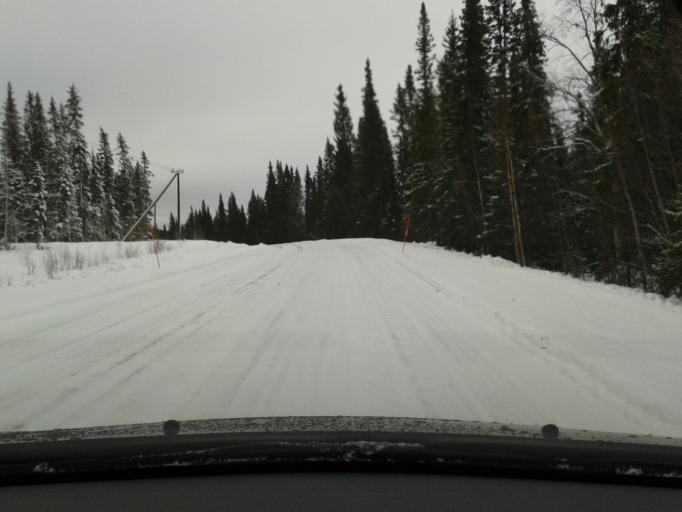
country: SE
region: Vaesterbotten
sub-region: Vilhelmina Kommun
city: Sjoberg
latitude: 65.2282
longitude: 15.8983
